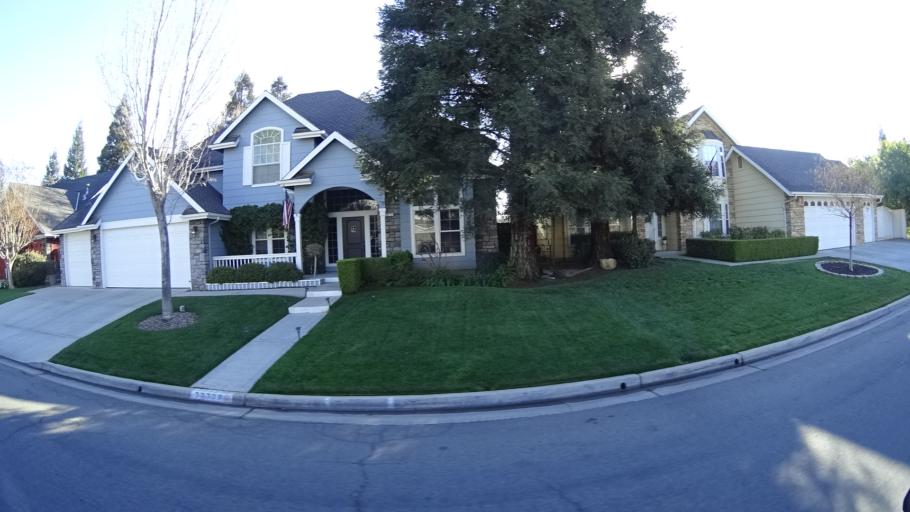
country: US
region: California
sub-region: Fresno County
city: Clovis
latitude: 36.8416
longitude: -119.7428
